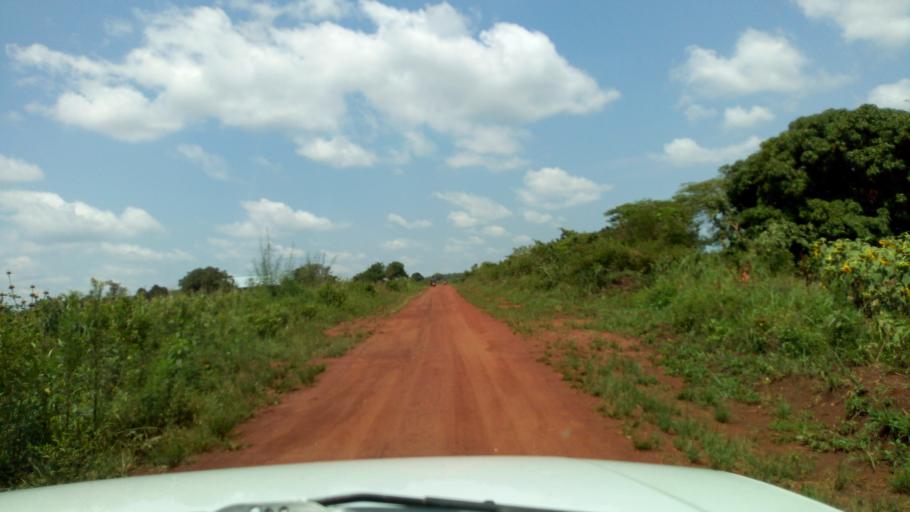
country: UG
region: Western Region
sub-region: Masindi District
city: Masindi
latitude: 1.7340
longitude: 31.8814
